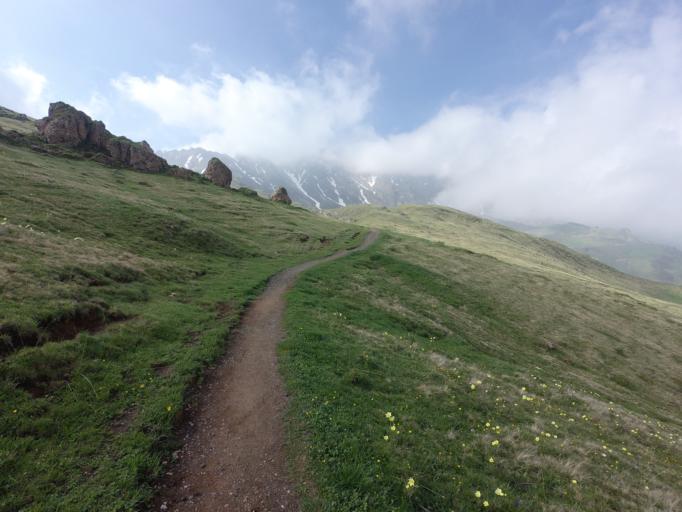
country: IT
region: Trentino-Alto Adige
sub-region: Bolzano
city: Ortisei
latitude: 46.5143
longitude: 11.6347
